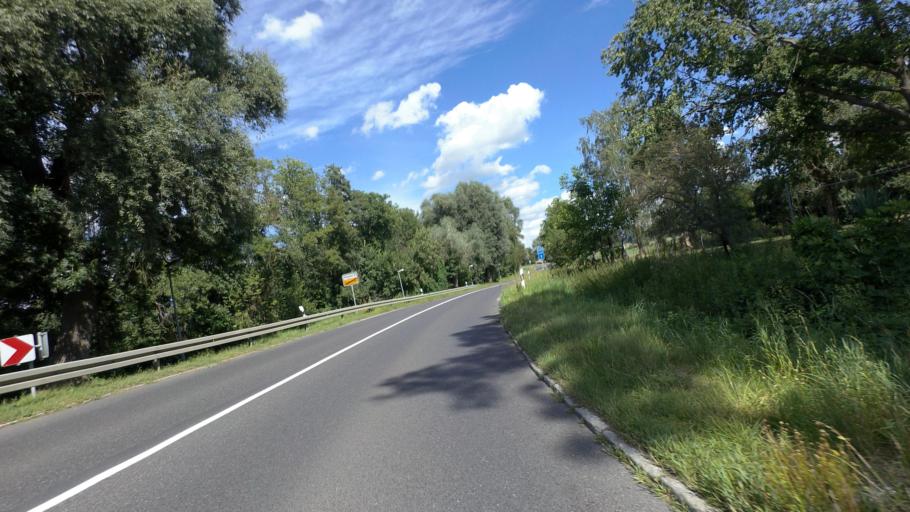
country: DE
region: Brandenburg
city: Wustermark
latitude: 52.5376
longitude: 12.9297
